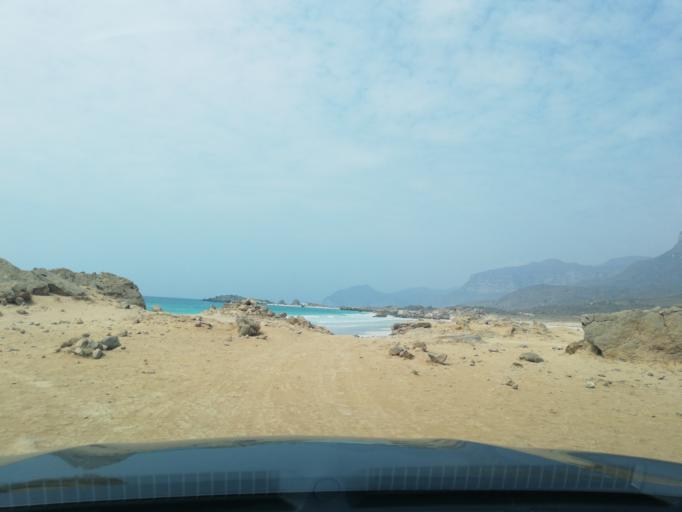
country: OM
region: Zufar
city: Salalah
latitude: 16.8343
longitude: 53.7145
